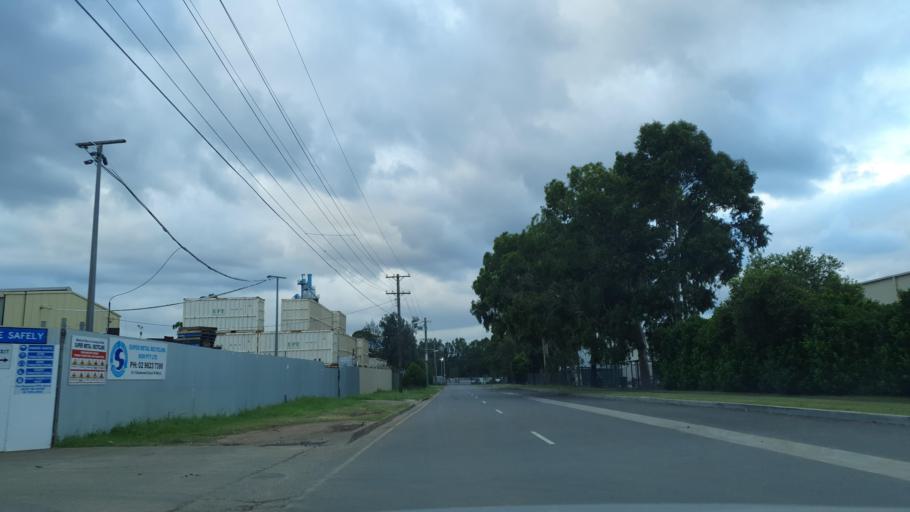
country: AU
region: New South Wales
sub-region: Penrith Municipality
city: Werrington County
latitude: -33.7391
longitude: 150.7673
